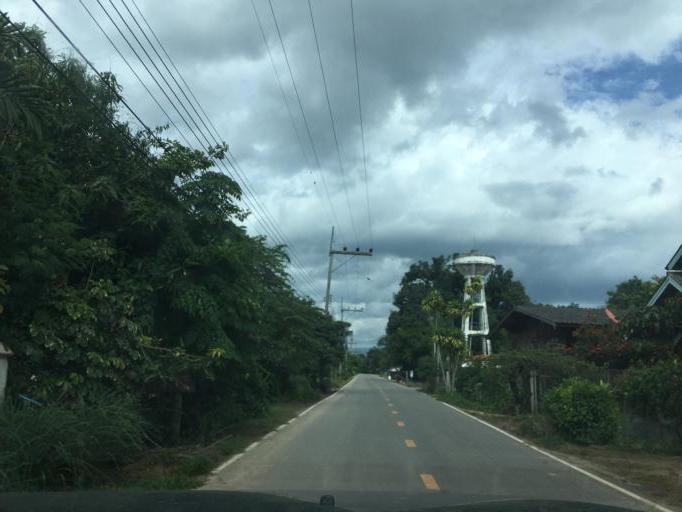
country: TH
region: Chiang Rai
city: Wiang Pa Pao
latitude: 19.2333
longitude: 99.4957
